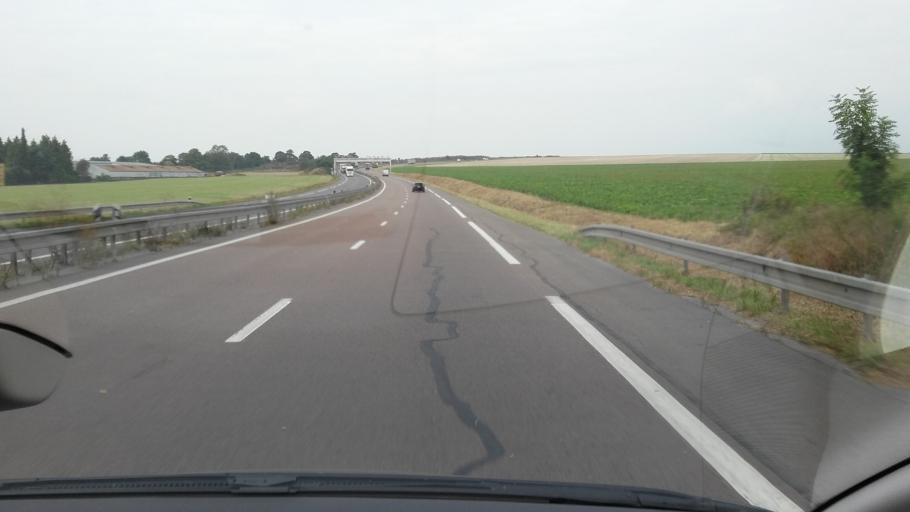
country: FR
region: Champagne-Ardenne
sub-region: Departement de la Marne
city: Warmeriville
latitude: 49.3574
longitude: 4.2072
